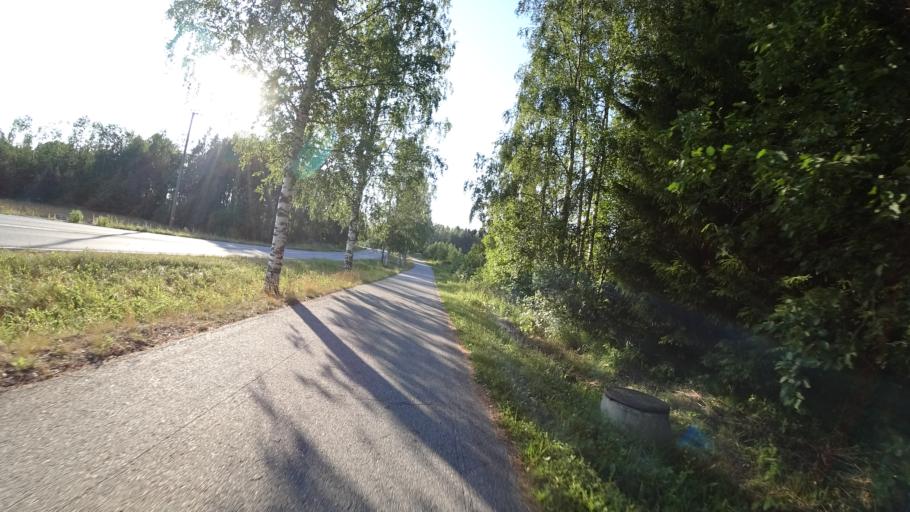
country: FI
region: Pirkanmaa
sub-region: Tampere
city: Nokia
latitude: 61.4687
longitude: 23.3961
